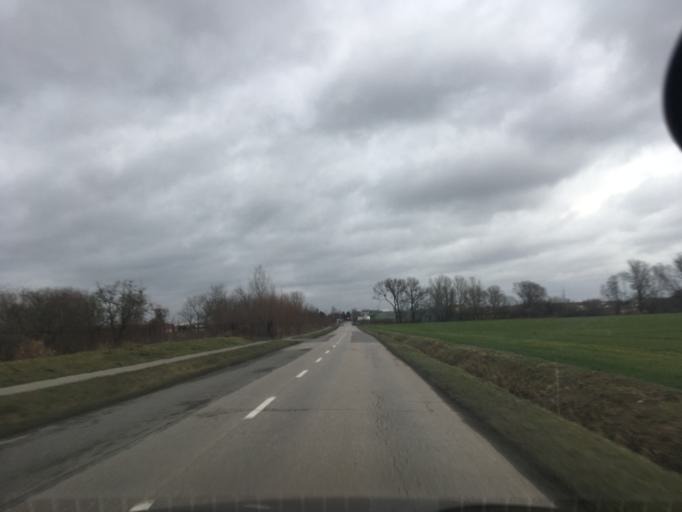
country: PL
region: Masovian Voivodeship
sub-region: Powiat pruszkowski
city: Rybie
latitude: 52.1313
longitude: 20.9692
